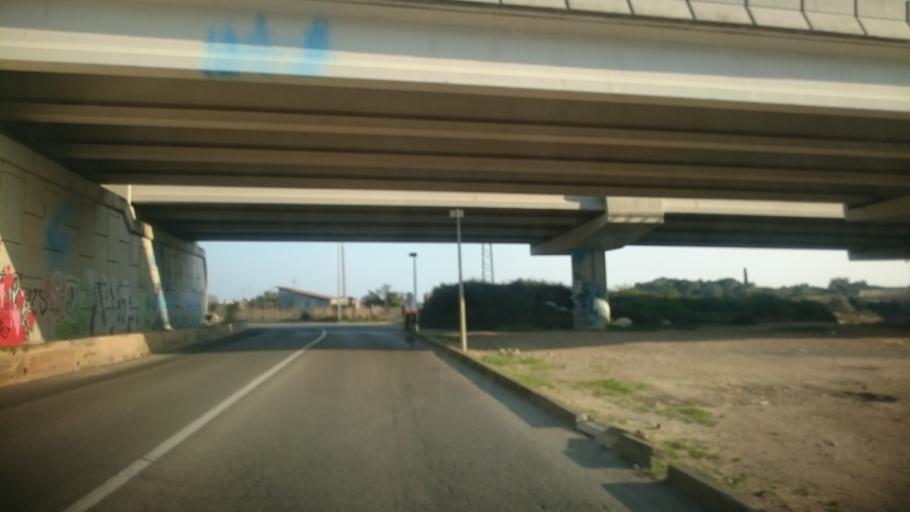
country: ES
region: Catalonia
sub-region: Provincia de Barcelona
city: Cubelles
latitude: 41.2139
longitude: 1.6642
